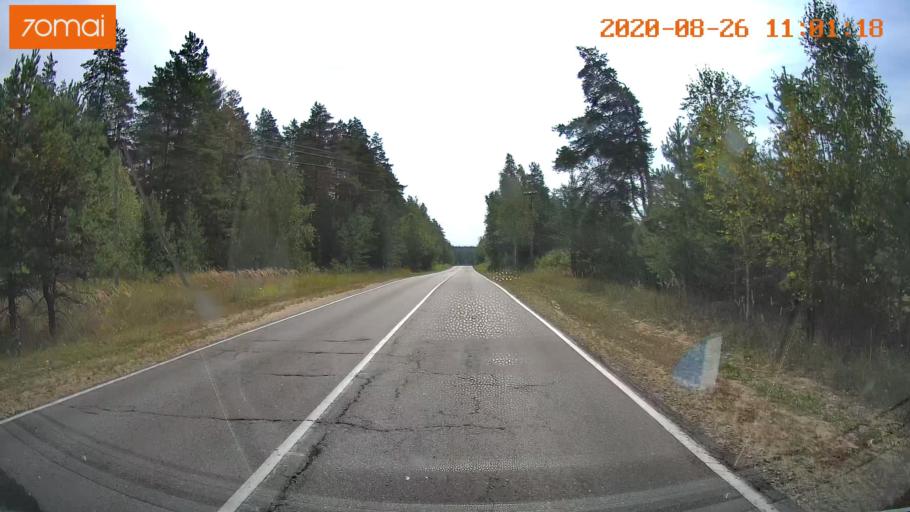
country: RU
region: Rjazan
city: Izhevskoye
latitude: 54.5646
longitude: 41.2230
